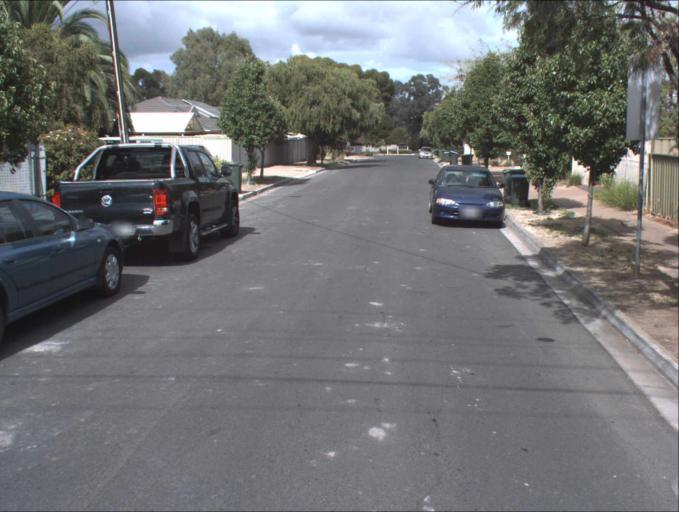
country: AU
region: South Australia
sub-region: Port Adelaide Enfield
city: Gilles Plains
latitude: -34.8490
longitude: 138.6604
